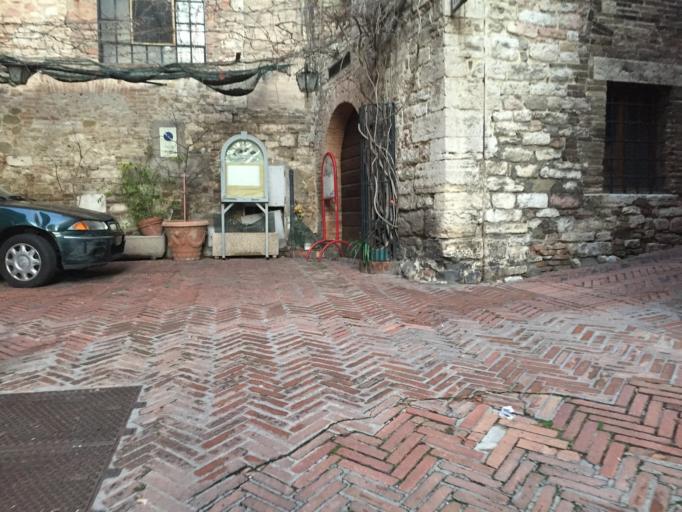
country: IT
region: Umbria
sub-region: Provincia di Perugia
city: Perugia
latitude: 43.1117
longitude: 12.3863
